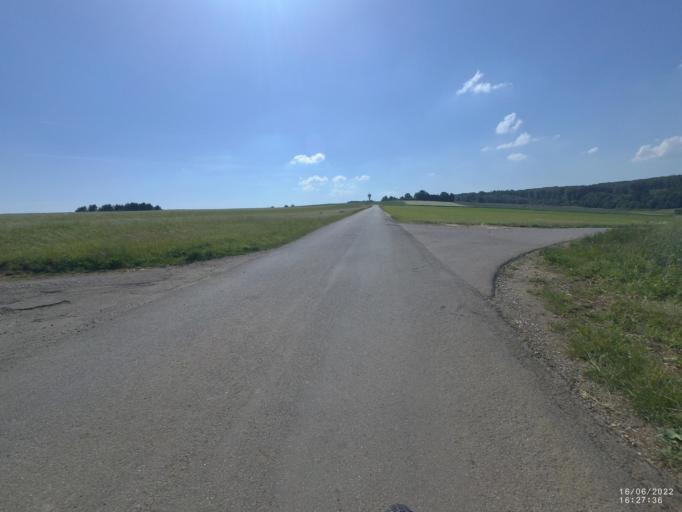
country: DE
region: Baden-Wuerttemberg
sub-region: Regierungsbezirk Stuttgart
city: Gerstetten
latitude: 48.6209
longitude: 10.0539
